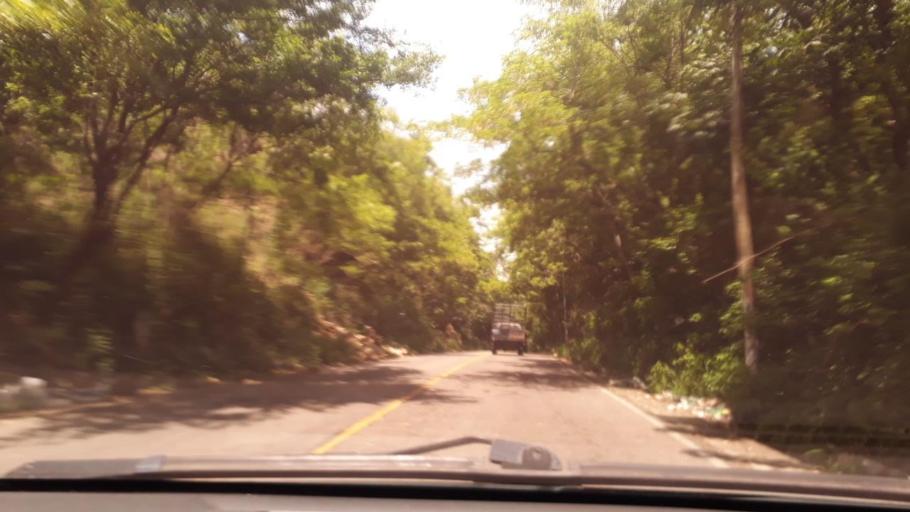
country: GT
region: Jutiapa
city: Jalpatagua
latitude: 14.1629
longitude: -90.0510
